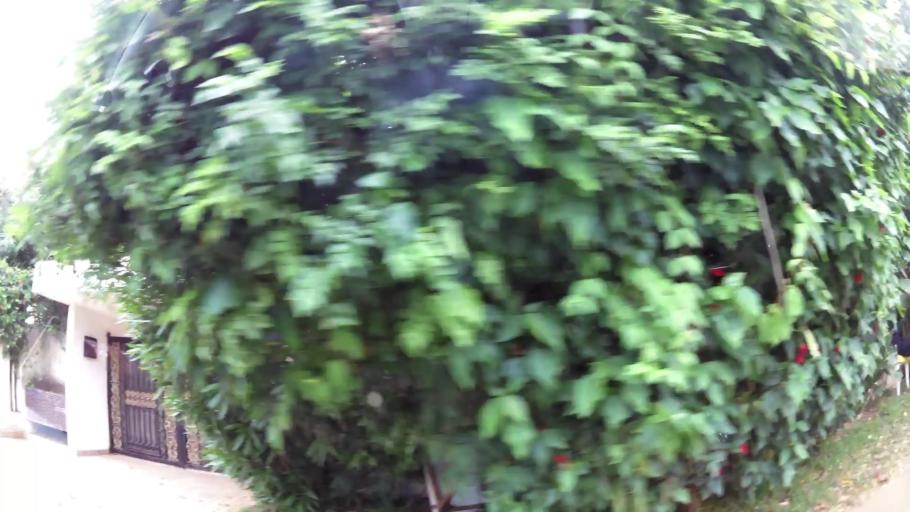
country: MA
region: Rabat-Sale-Zemmour-Zaer
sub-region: Rabat
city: Rabat
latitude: 33.9660
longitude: -6.8156
